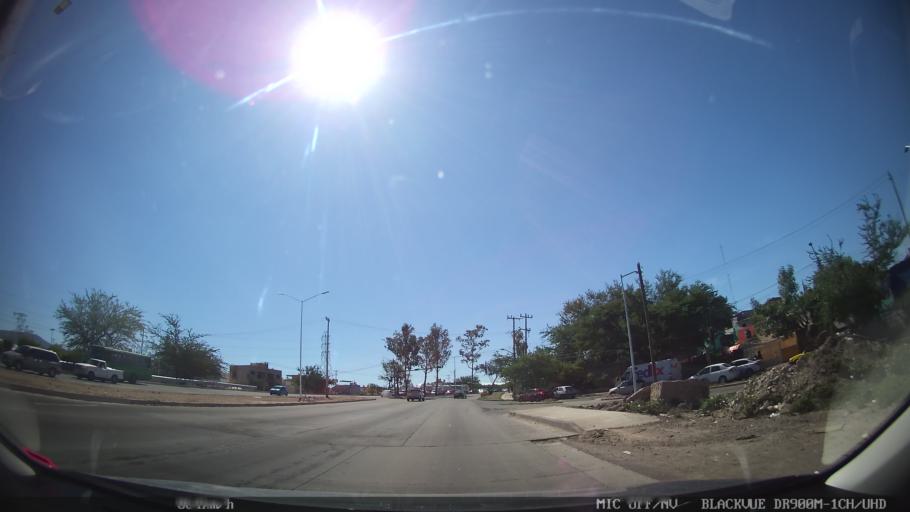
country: MX
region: Jalisco
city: Tlaquepaque
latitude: 20.7039
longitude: -103.2841
